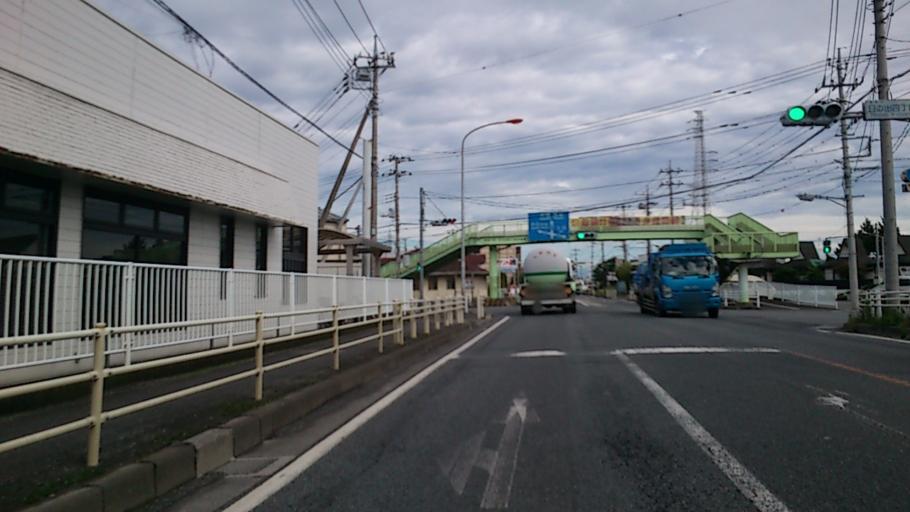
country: JP
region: Saitama
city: Honjo
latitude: 36.2361
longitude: 139.2076
